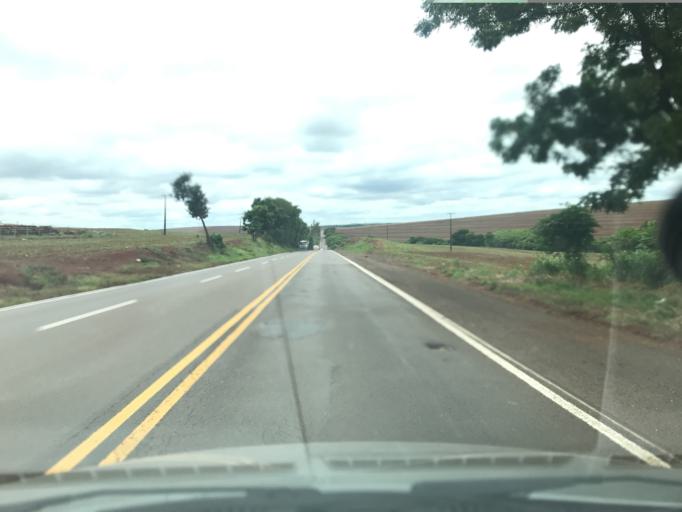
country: BR
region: Parana
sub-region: Terra Boa
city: Terra Boa
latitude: -23.5998
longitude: -52.3976
